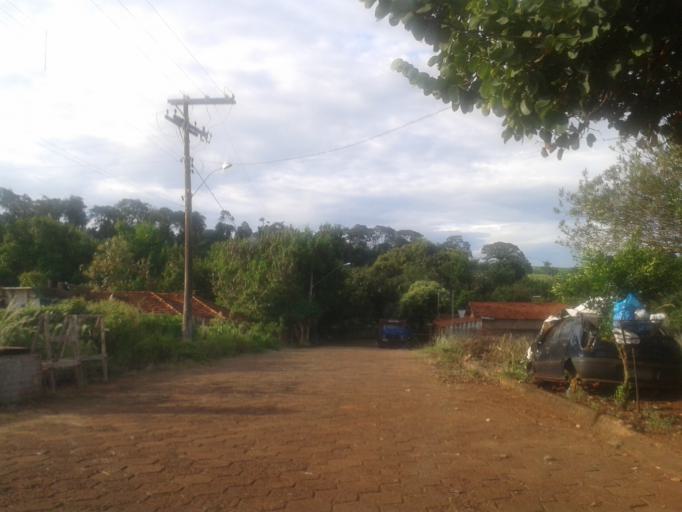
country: BR
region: Minas Gerais
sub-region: Capinopolis
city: Capinopolis
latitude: -18.6765
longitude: -49.5682
